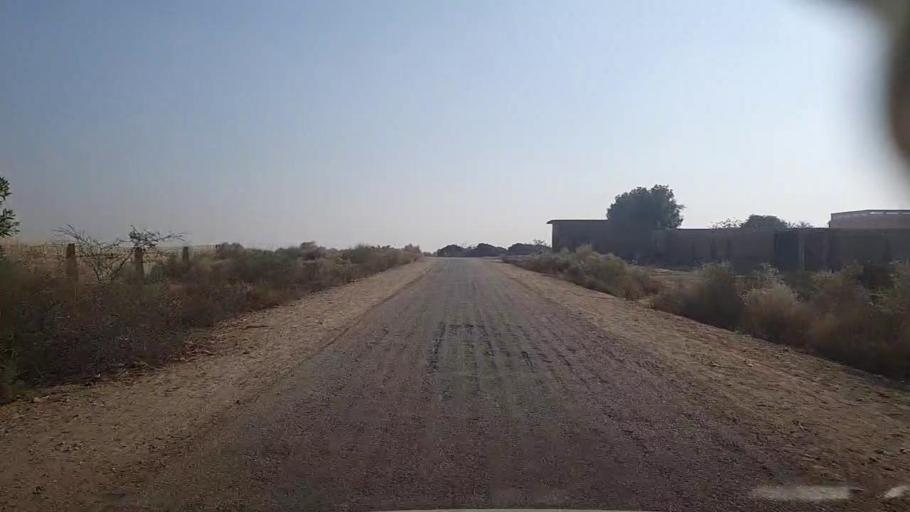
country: PK
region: Sindh
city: Kandiari
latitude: 26.8249
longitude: 68.4892
